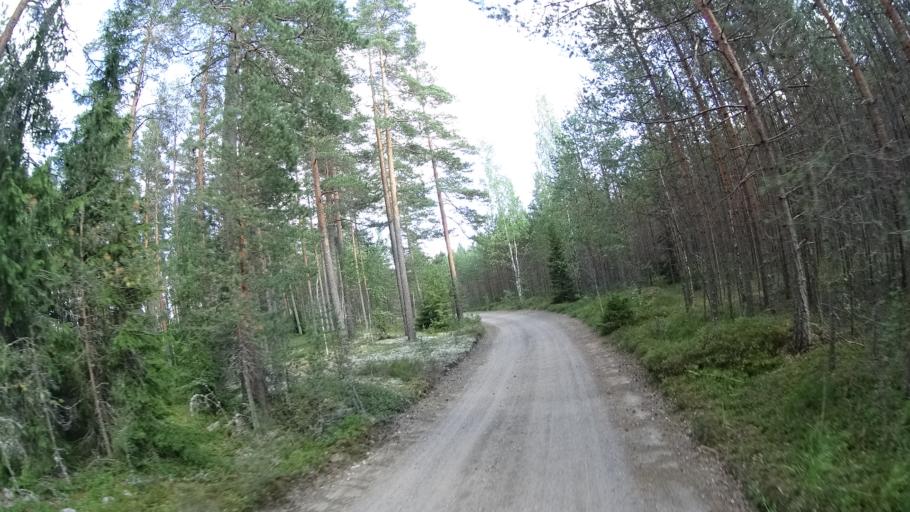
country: FI
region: Uusimaa
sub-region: Helsinki
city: Kaerkoelae
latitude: 60.7319
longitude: 24.0410
